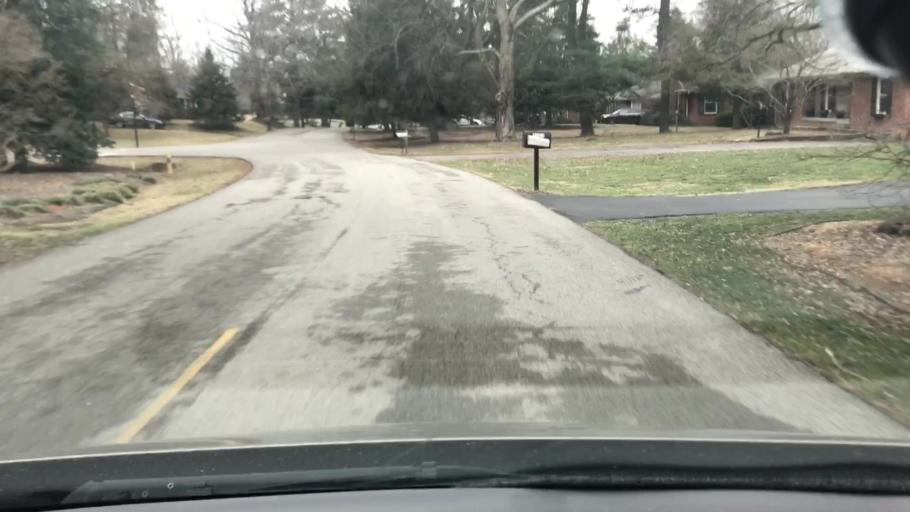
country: US
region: Kentucky
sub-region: Jefferson County
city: Barbourmeade
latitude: 38.2953
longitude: -85.6047
